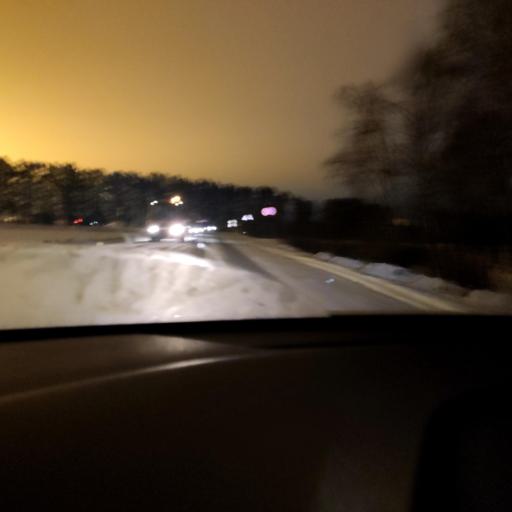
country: RU
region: Tatarstan
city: Osinovo
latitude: 55.8871
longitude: 48.8913
